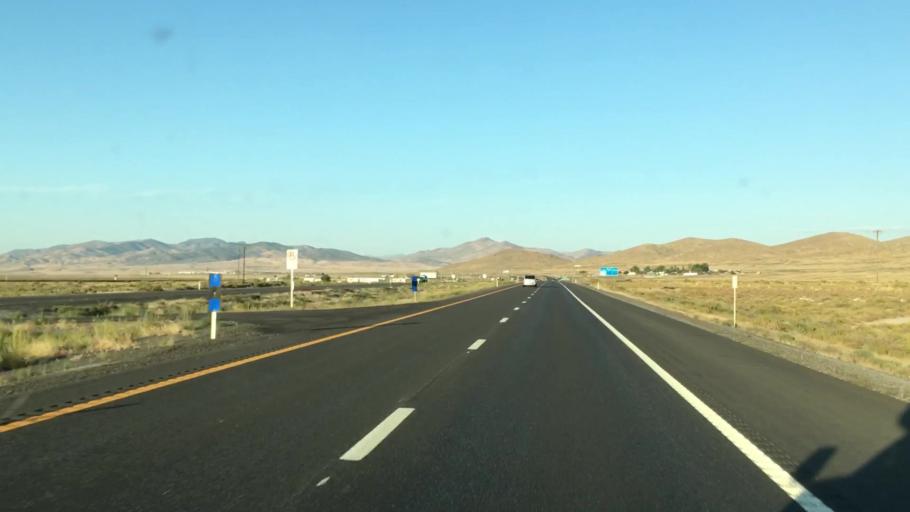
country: US
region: Nevada
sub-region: Humboldt County
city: Winnemucca
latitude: 40.6739
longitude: -118.0855
